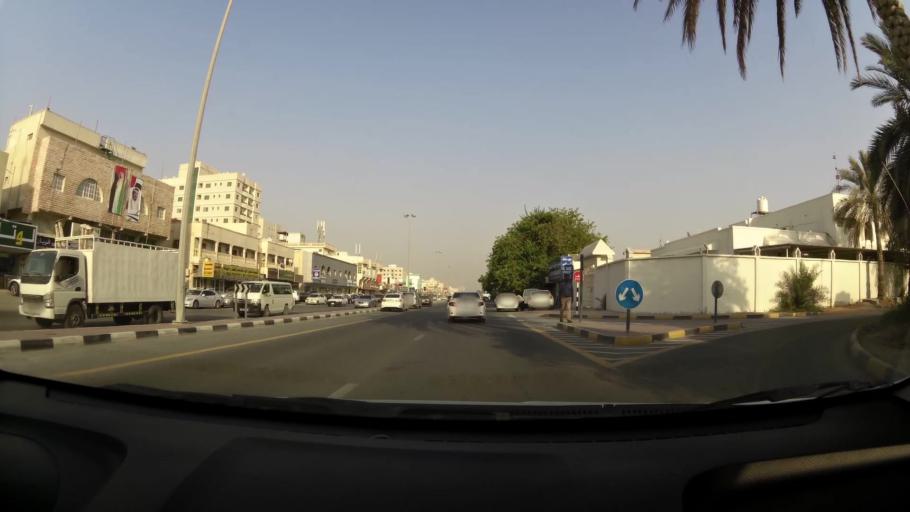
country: AE
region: Ajman
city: Ajman
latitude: 25.3862
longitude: 55.4398
